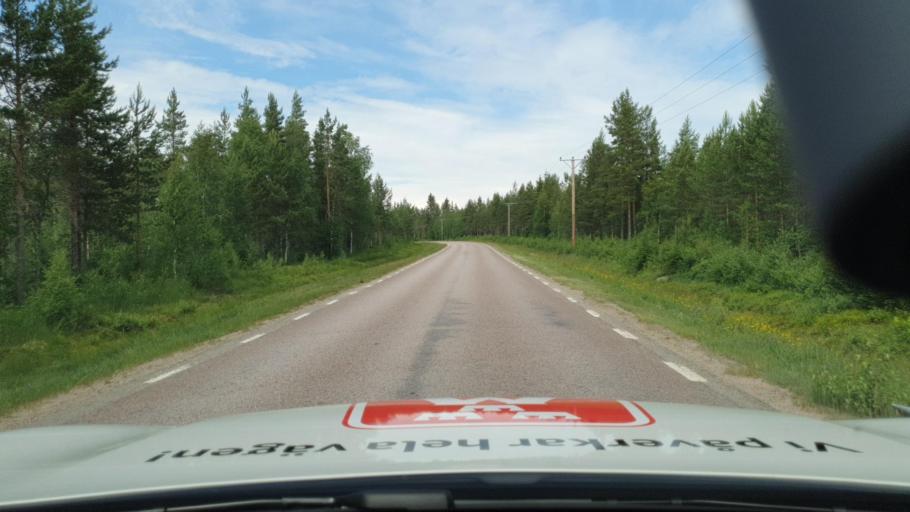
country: NO
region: Hedmark
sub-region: Grue
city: Kirkenaer
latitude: 60.7113
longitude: 12.6152
